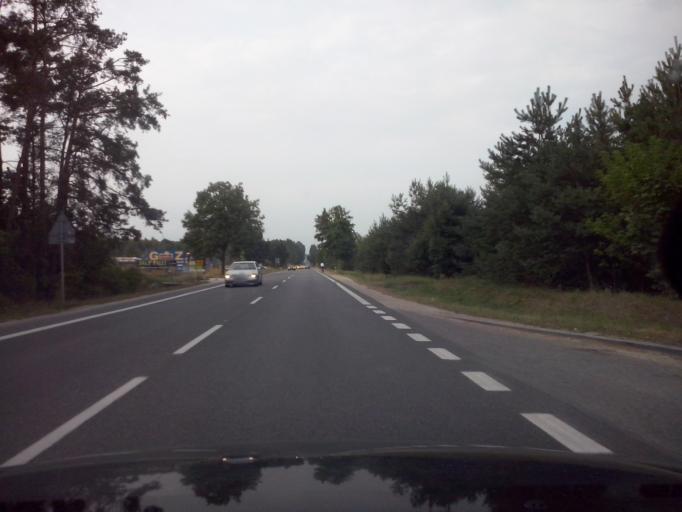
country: PL
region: Swietokrzyskie
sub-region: Powiat kielecki
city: Morawica
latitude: 50.7579
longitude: 20.6185
